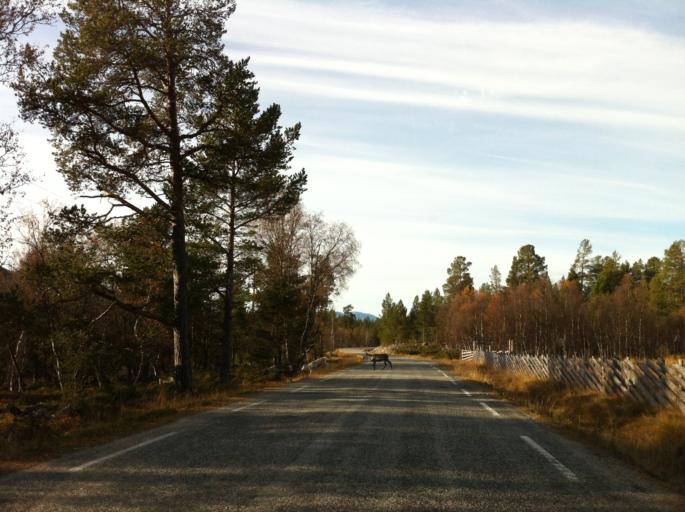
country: NO
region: Hedmark
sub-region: Engerdal
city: Engerdal
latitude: 62.1114
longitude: 12.0185
